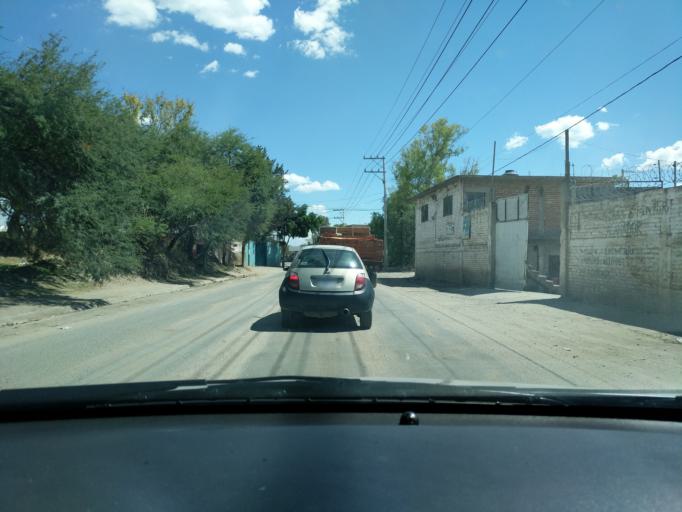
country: MX
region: Guanajuato
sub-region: Leon
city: Ladrilleras del Refugio
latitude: 21.0661
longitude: -101.5534
